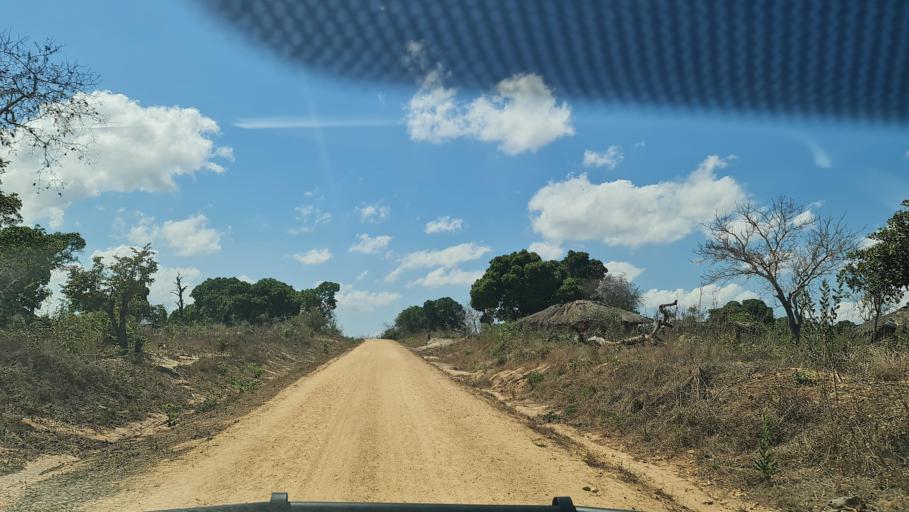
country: MZ
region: Nampula
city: Nacala
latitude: -14.1747
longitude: 40.2056
